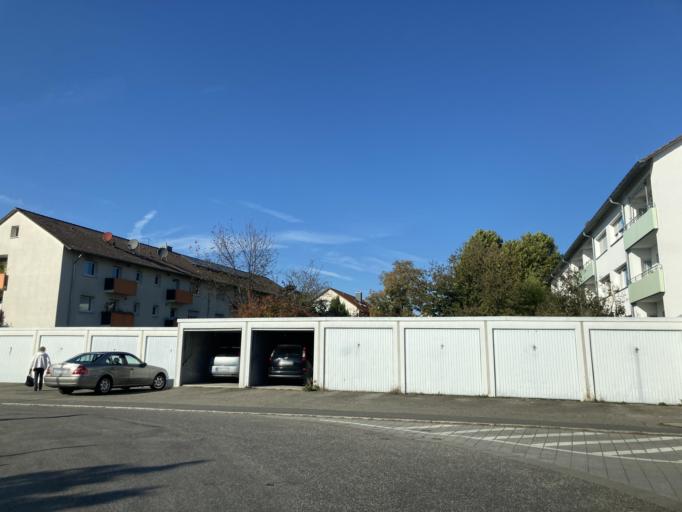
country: DE
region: Baden-Wuerttemberg
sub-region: Freiburg Region
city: Heitersheim
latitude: 47.8747
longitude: 7.6486
